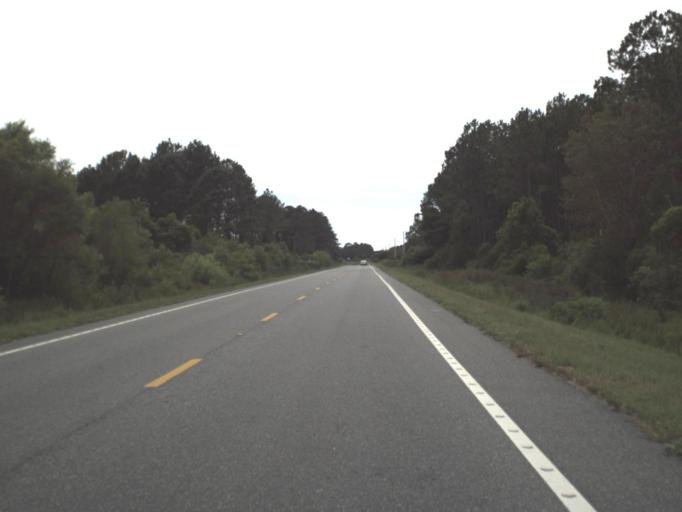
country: US
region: Florida
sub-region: Taylor County
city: Perry
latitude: 30.1228
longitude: -83.3951
